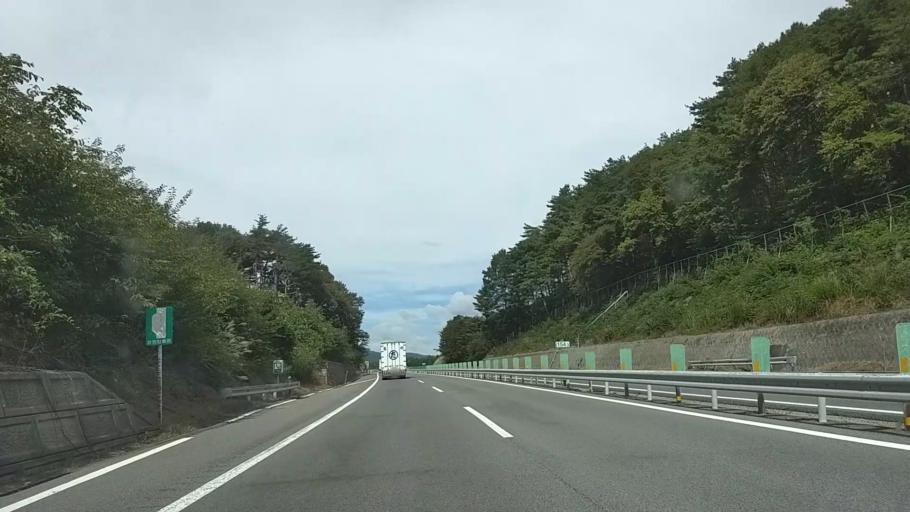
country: JP
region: Nagano
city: Chino
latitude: 35.9038
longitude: 138.2633
